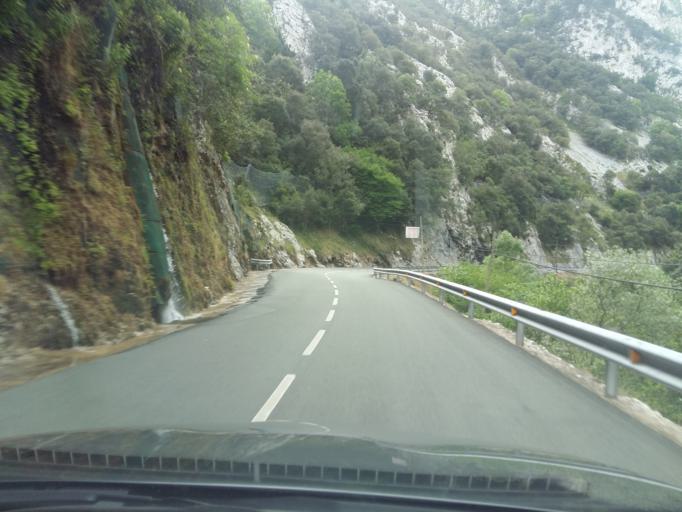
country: ES
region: Cantabria
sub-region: Provincia de Cantabria
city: Tresviso
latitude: 43.3057
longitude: -4.6057
